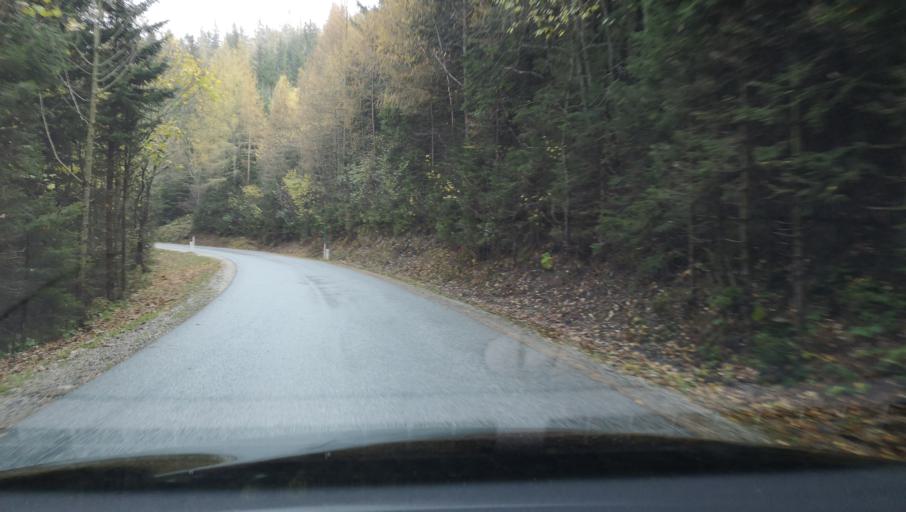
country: AT
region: Styria
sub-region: Politischer Bezirk Weiz
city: Gasen
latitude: 47.3561
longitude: 15.5888
